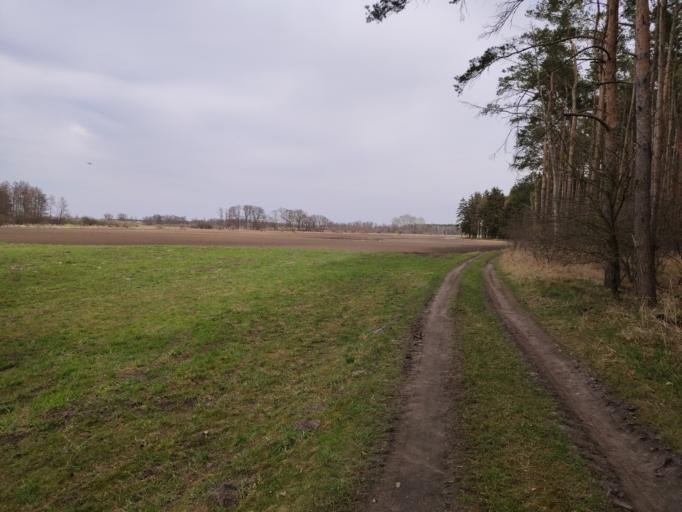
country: PL
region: Greater Poland Voivodeship
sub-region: Powiat sredzki
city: Sroda Wielkopolska
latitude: 52.1471
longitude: 17.2745
